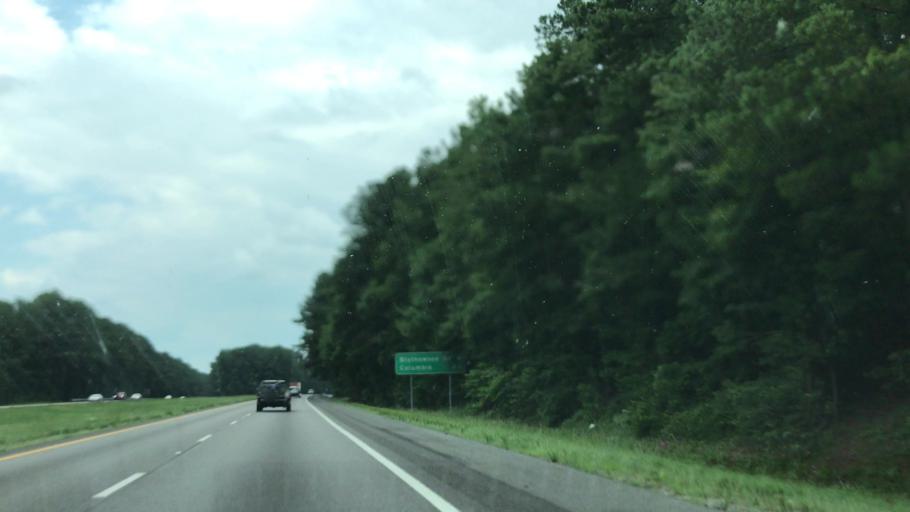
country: US
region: South Carolina
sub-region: Richland County
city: Blythewood
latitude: 34.2663
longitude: -80.9981
